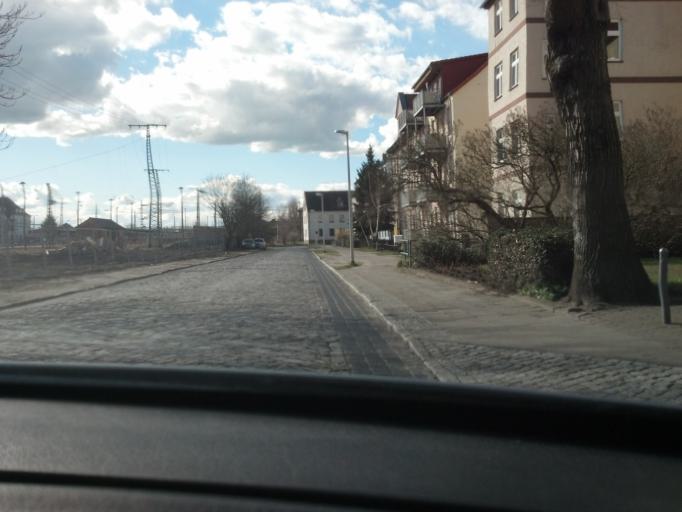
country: DE
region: Mecklenburg-Vorpommern
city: Neubrandenburg
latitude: 53.5620
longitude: 13.2655
